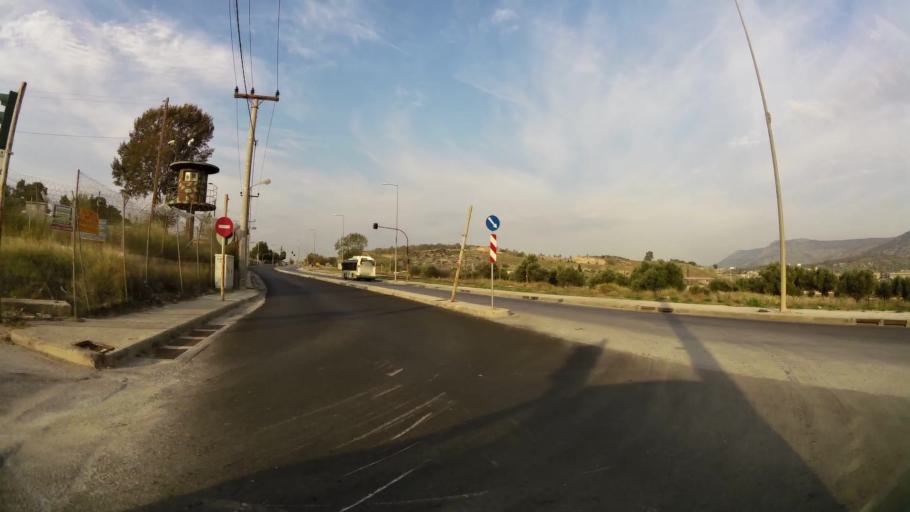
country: GR
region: Attica
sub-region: Nomarchia Dytikis Attikis
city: Ano Liosia
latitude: 38.0689
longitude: 23.6787
